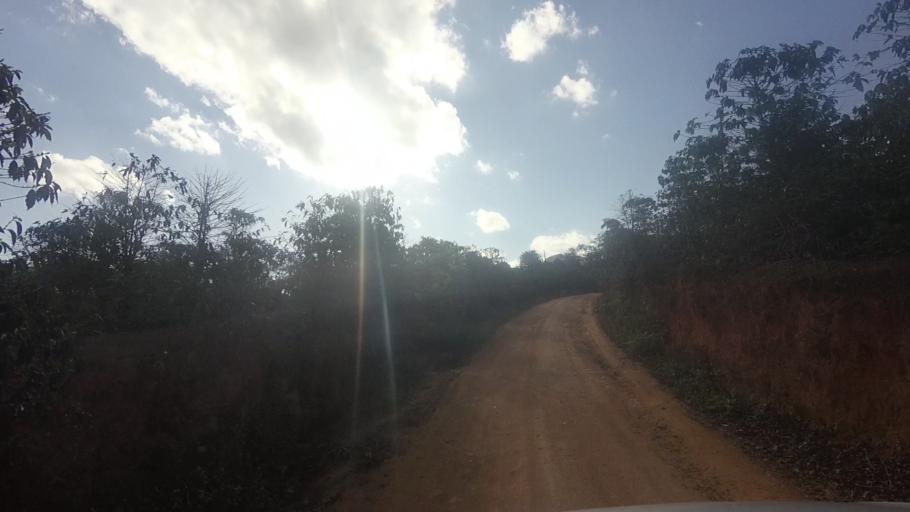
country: BR
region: Espirito Santo
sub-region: Sao Jose Do Calcado
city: Sao Jose do Calcado
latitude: -20.9869
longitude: -41.5213
